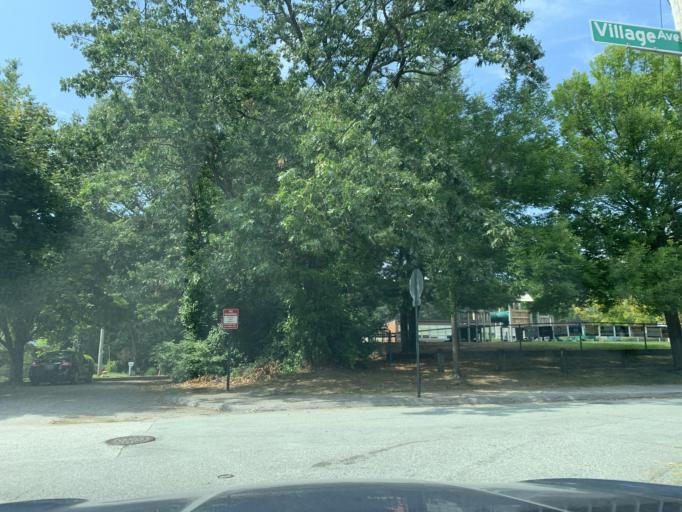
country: US
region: Rhode Island
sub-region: Providence County
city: Johnston
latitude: 41.7870
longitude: -71.4828
